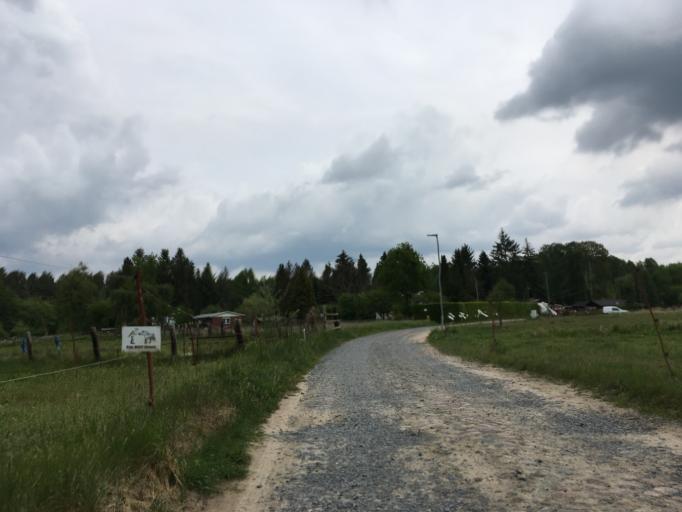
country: DE
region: Brandenburg
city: Marienwerder
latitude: 52.8451
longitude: 13.6094
